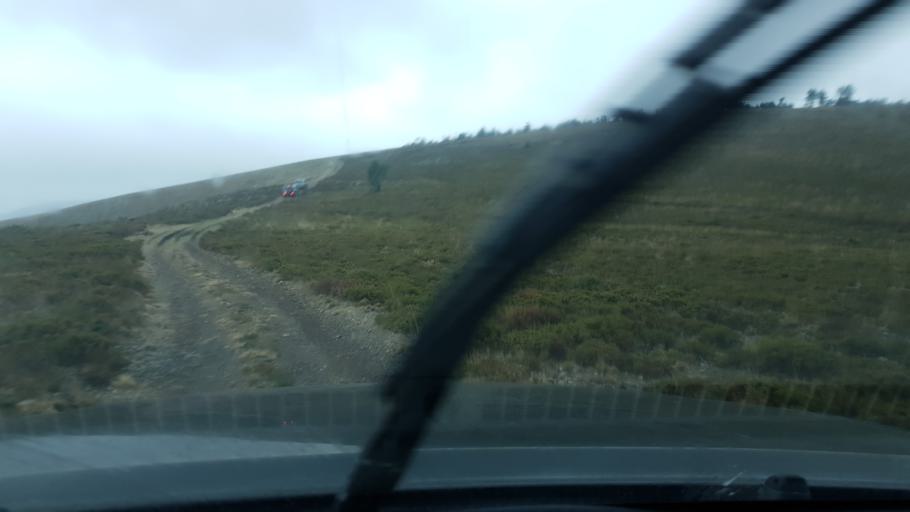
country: PT
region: Viseu
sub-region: Sao Pedro do Sul
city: Sao Pedro do Sul
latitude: 40.8633
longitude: -8.0938
